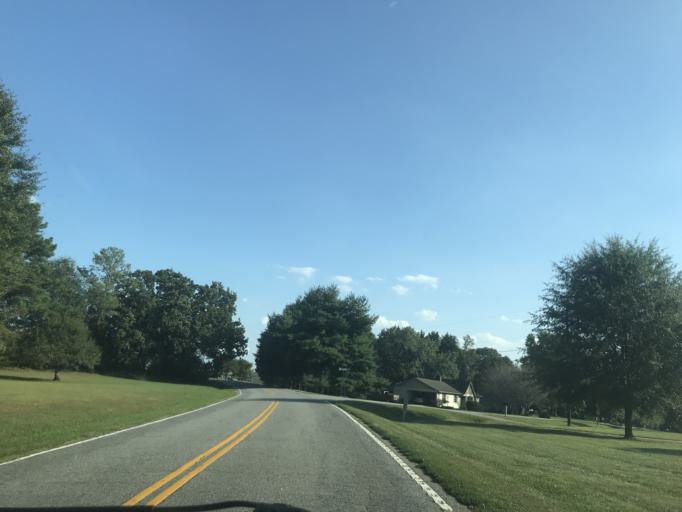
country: US
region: South Carolina
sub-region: Cherokee County
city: Gaffney
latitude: 35.1306
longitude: -81.6904
